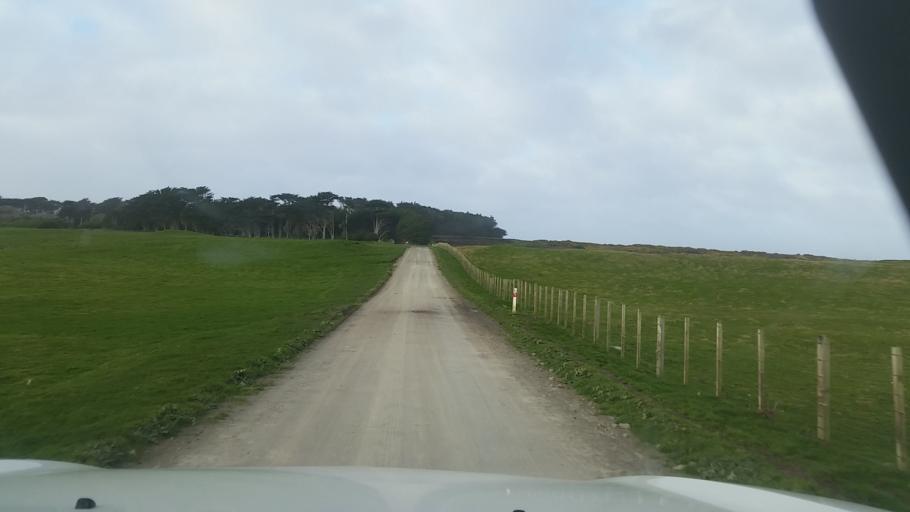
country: NZ
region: Chatham Islands
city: Waitangi
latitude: -43.7379
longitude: -176.2544
